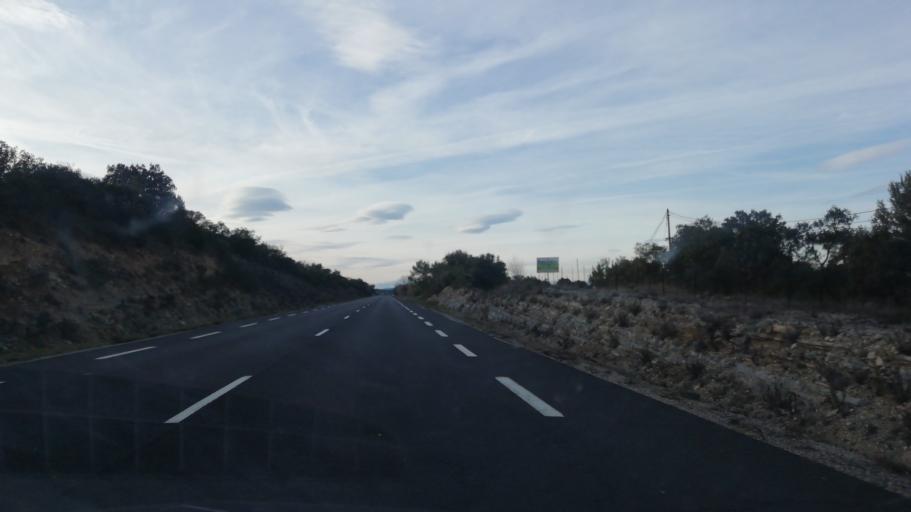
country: FR
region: Languedoc-Roussillon
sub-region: Departement du Gard
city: Clarensac
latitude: 43.8574
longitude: 4.2372
